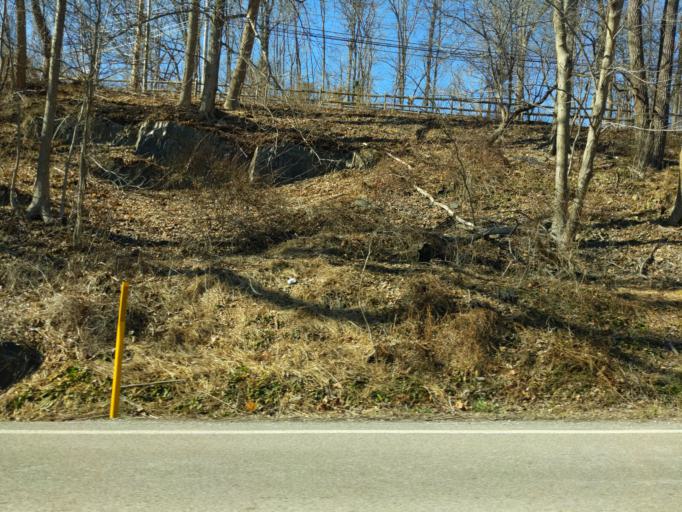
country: US
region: Pennsylvania
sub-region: Montgomery County
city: Red Hill
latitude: 40.3406
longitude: -75.4752
